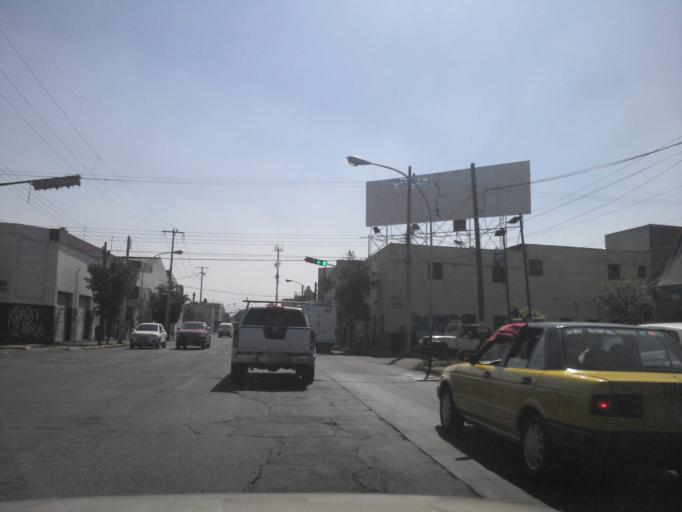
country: MX
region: Jalisco
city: Guadalajara
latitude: 20.6900
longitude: -103.3589
